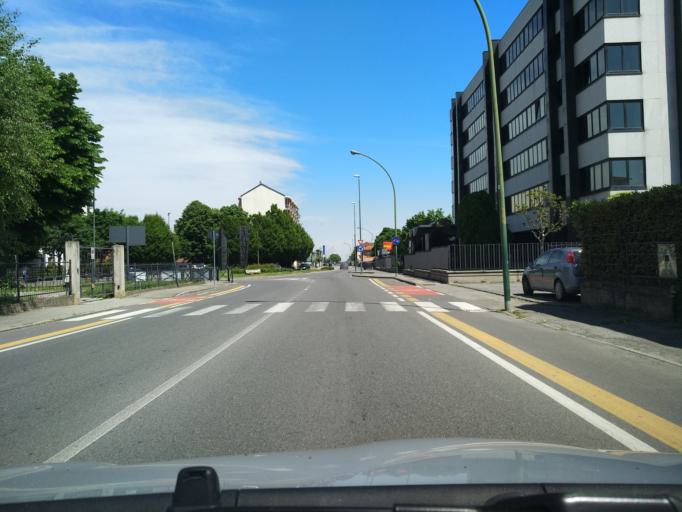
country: IT
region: Piedmont
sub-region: Provincia di Torino
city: Pinerolo
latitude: 44.8876
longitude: 7.3501
